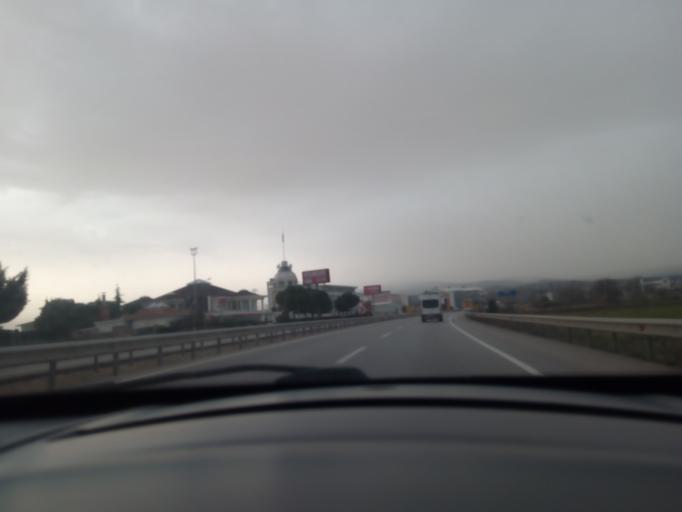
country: TR
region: Bursa
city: Tatkavakli
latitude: 40.0397
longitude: 28.3776
